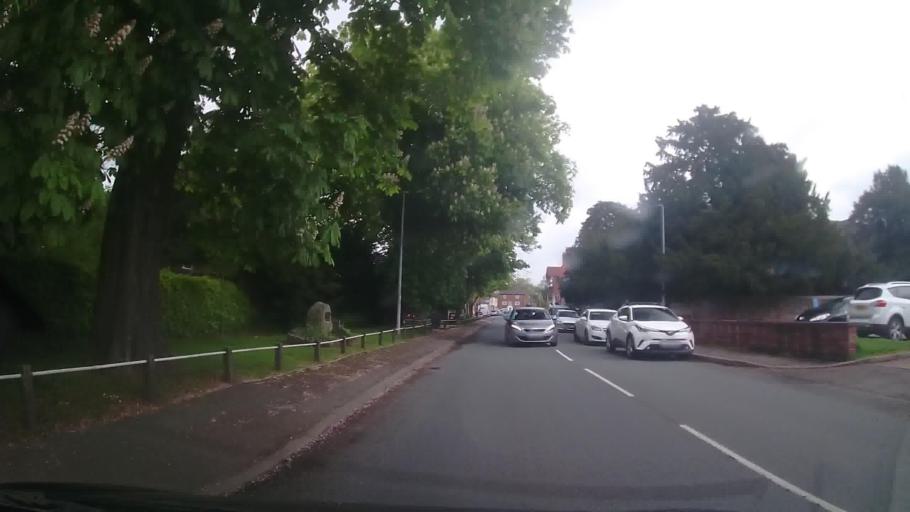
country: GB
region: Wales
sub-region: Wrexham
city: Overton
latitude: 52.9684
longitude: -2.9360
